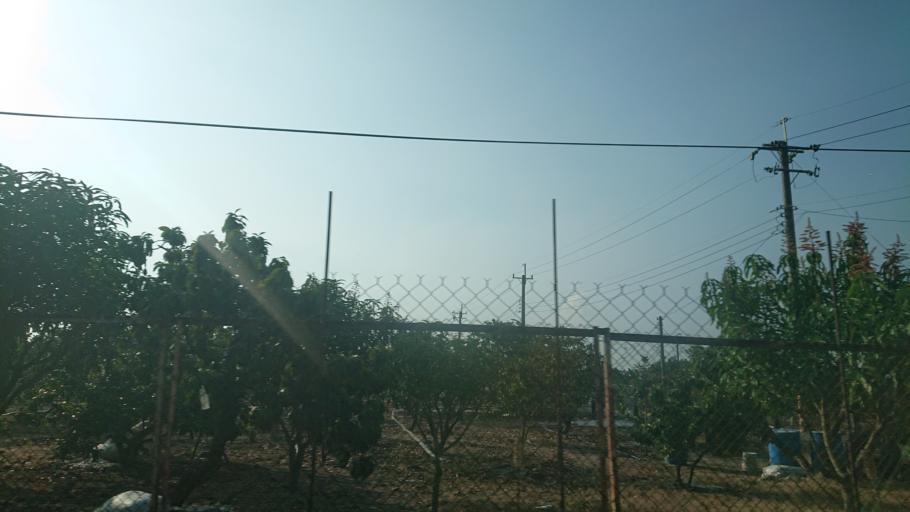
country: TW
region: Taiwan
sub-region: Tainan
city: Tainan
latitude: 23.1528
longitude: 120.2488
